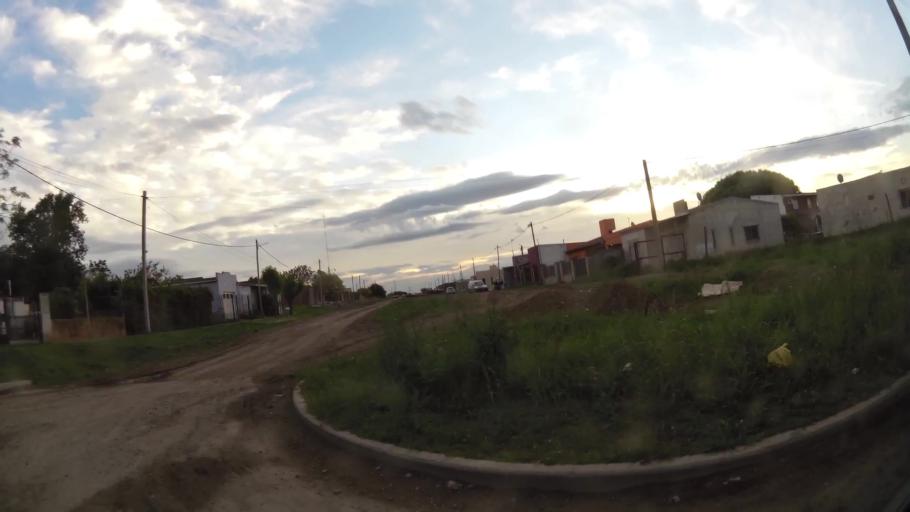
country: AR
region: Buenos Aires
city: San Nicolas de los Arroyos
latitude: -33.3169
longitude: -60.2451
